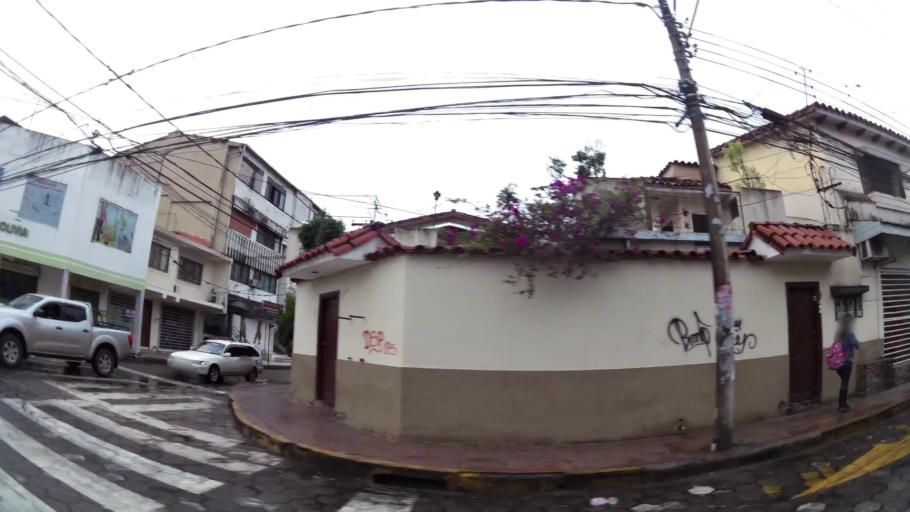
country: BO
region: Santa Cruz
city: Santa Cruz de la Sierra
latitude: -17.7831
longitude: -63.1749
